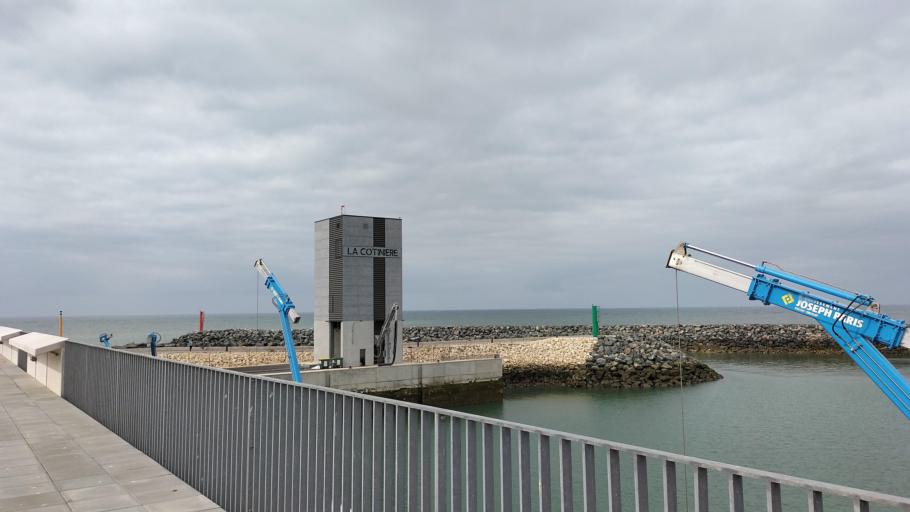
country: FR
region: Poitou-Charentes
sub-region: Departement de la Charente-Maritime
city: Dolus-d'Oleron
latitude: 45.9113
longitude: -1.3260
